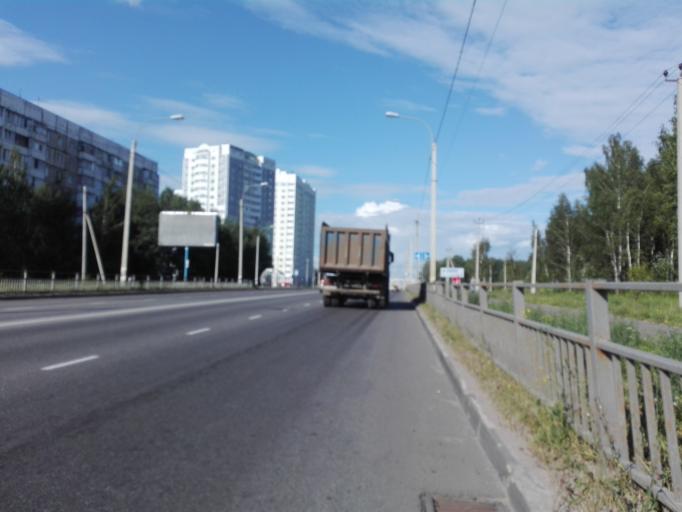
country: RU
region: Orjol
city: Orel
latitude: 53.0030
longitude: 36.1101
